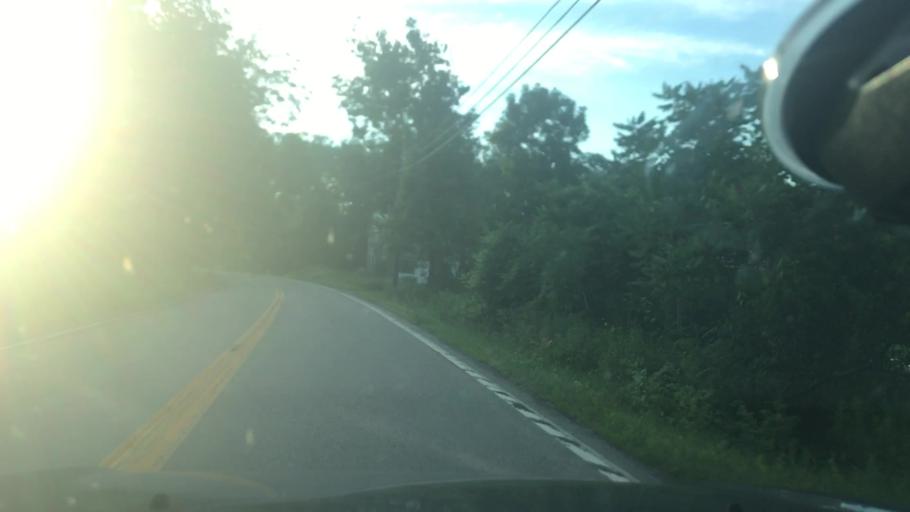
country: US
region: New York
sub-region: Otsego County
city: Unadilla
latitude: 42.3350
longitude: -75.2379
